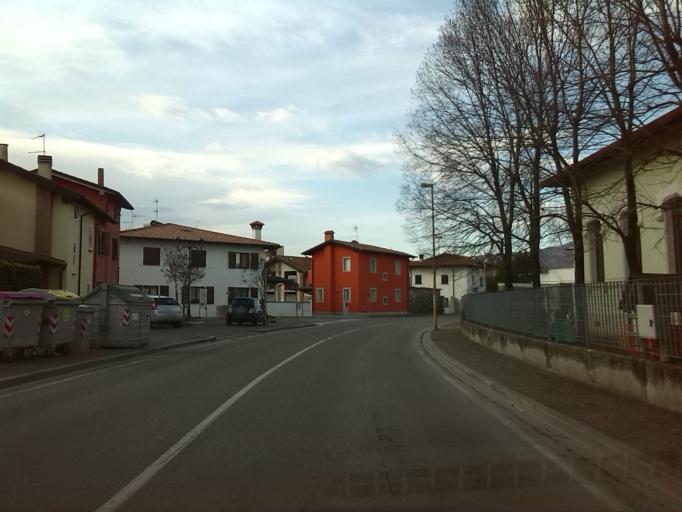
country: IT
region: Friuli Venezia Giulia
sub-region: Provincia di Udine
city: Cividale del Friuli
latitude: 46.0846
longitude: 13.4316
